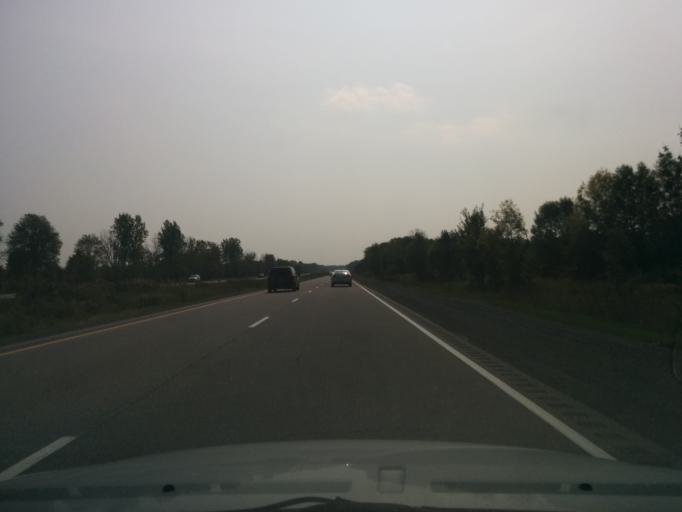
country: CA
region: Ontario
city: Bells Corners
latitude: 45.1766
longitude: -75.7056
